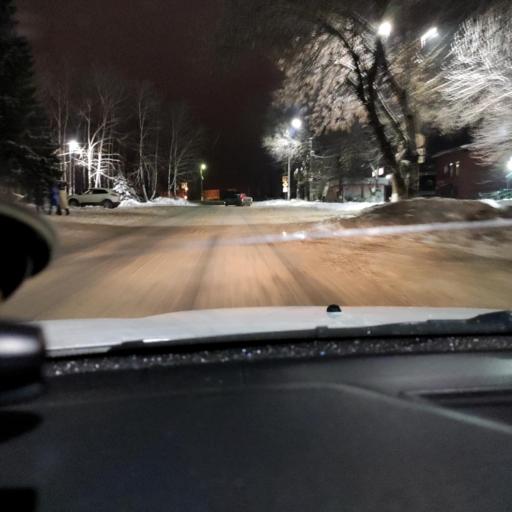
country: RU
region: Samara
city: Smyshlyayevka
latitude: 53.2531
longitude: 50.4798
